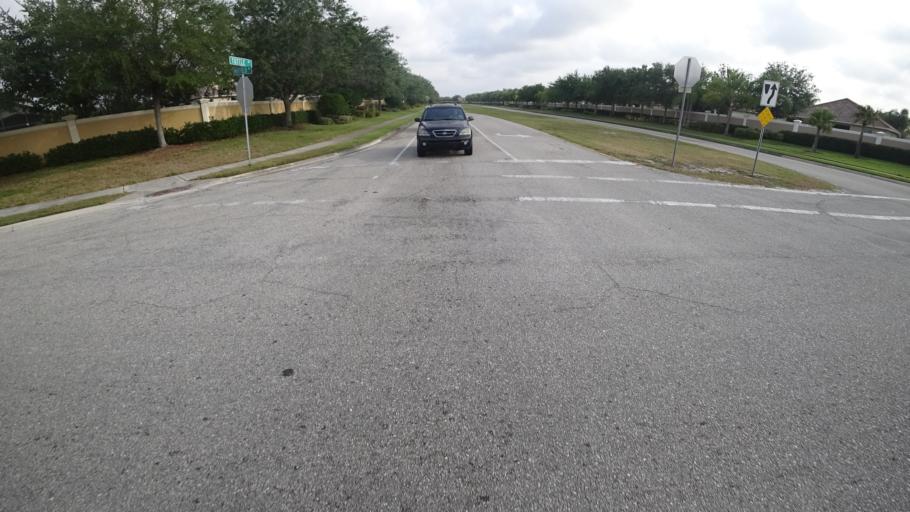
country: US
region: Florida
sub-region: Sarasota County
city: North Sarasota
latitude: 27.4197
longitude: -82.5132
